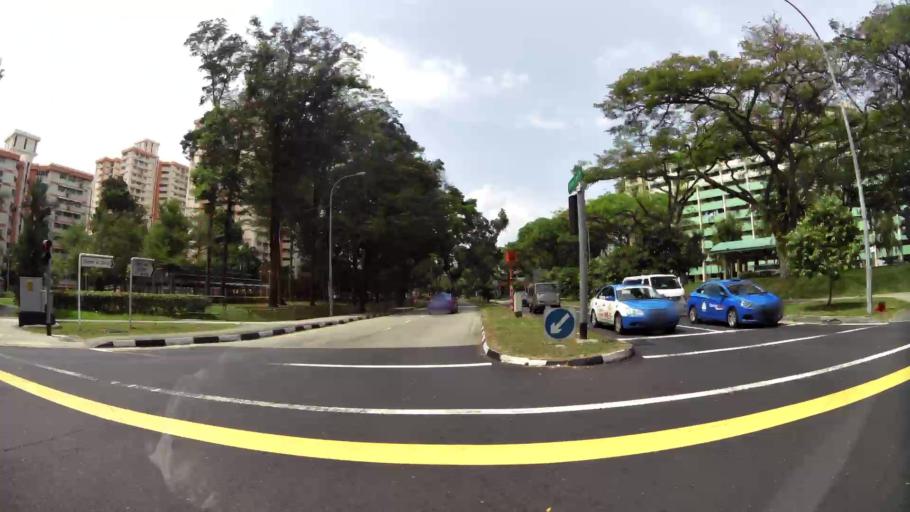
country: MY
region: Johor
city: Johor Bahru
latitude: 1.3459
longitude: 103.7159
